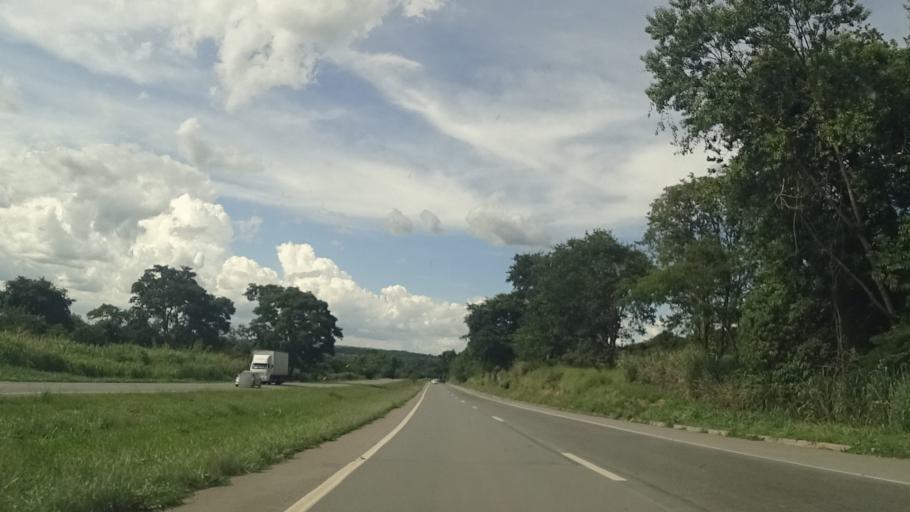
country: BR
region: Goias
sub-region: Piracanjuba
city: Piracanjuba
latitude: -17.2260
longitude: -49.2291
